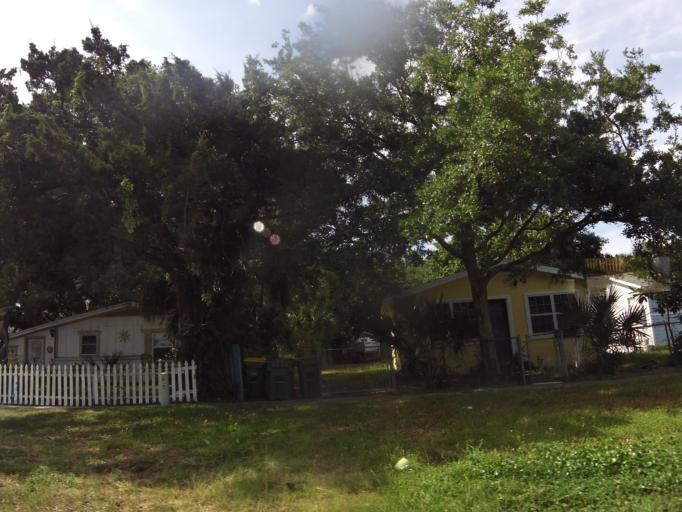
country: US
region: Florida
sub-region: Duval County
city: Jacksonville Beach
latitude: 30.2848
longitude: -81.3951
